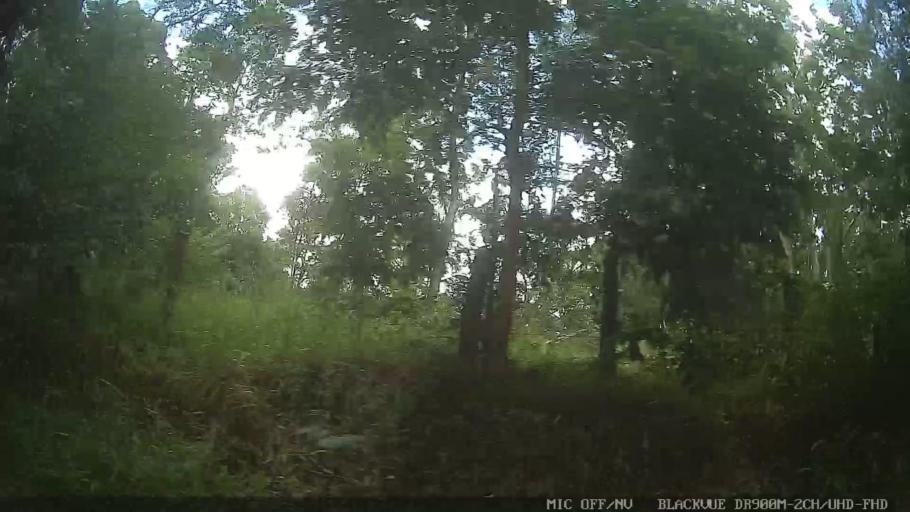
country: BR
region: Sao Paulo
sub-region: Braganca Paulista
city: Braganca Paulista
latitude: -23.0261
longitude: -46.4694
